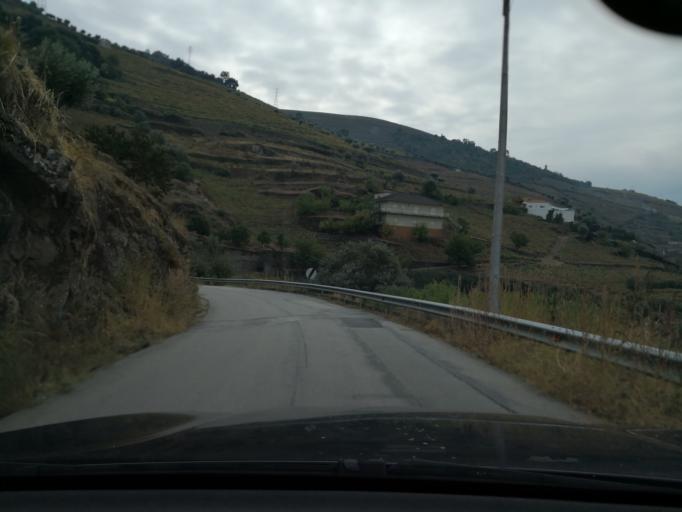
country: PT
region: Vila Real
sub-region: Peso da Regua
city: Peso da Regua
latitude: 41.1759
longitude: -7.7418
